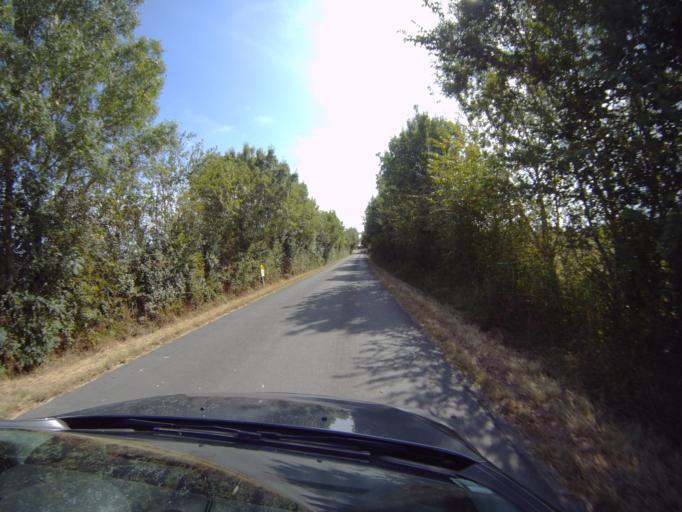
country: FR
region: Poitou-Charentes
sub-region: Departement des Deux-Sevres
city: Saint-Hilaire-la-Palud
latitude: 46.2730
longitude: -0.6578
